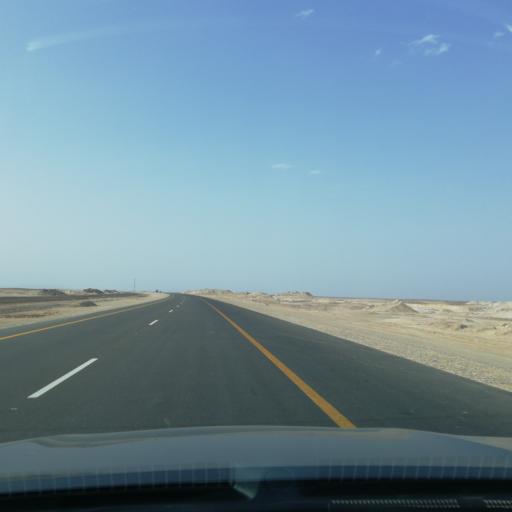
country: OM
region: Muhafazat ad Dakhiliyah
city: Adam
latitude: 22.1245
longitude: 57.5254
